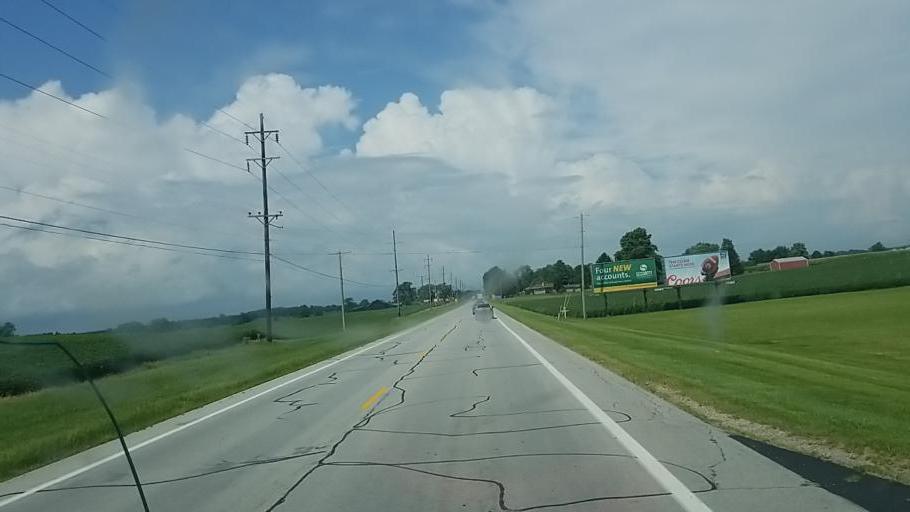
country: US
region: Ohio
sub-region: Champaign County
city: Urbana
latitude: 40.1500
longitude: -83.7462
